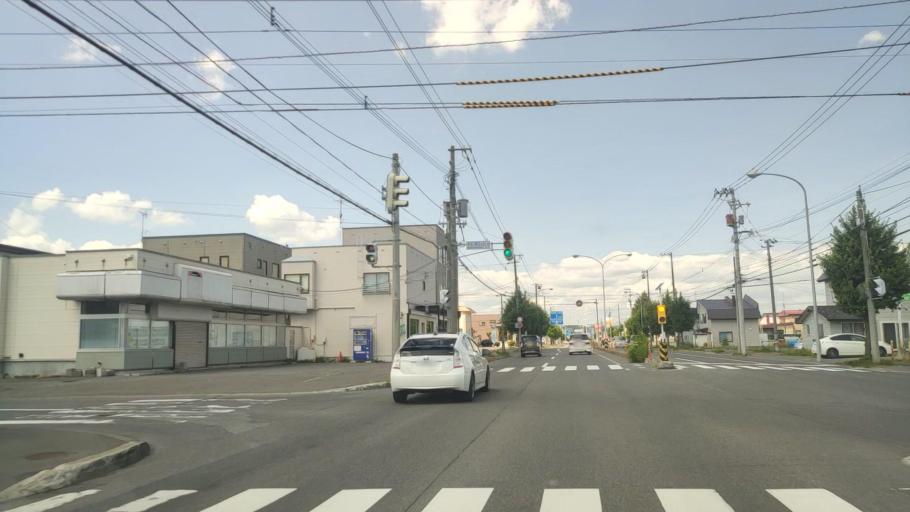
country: JP
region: Hokkaido
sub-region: Asahikawa-shi
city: Asahikawa
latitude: 43.8013
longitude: 142.3915
